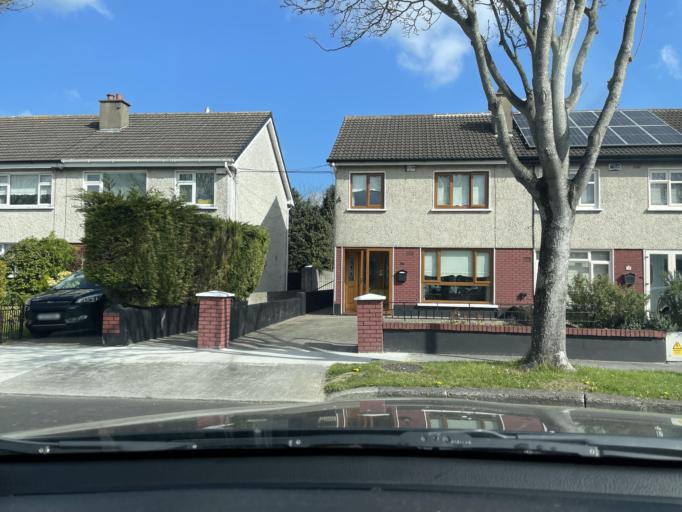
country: IE
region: Leinster
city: Clondalkin
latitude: 53.3287
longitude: -6.4039
